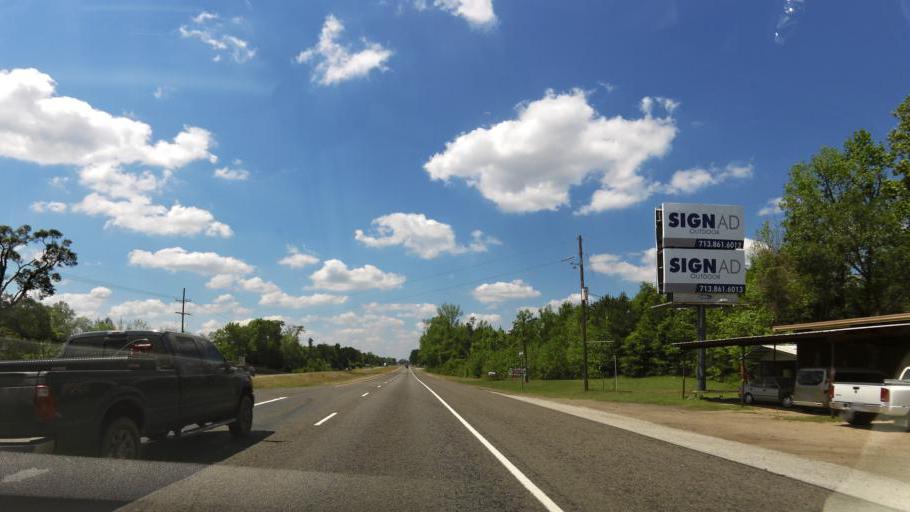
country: US
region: Texas
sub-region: San Jacinto County
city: Shepherd
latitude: 30.5303
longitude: -94.9764
